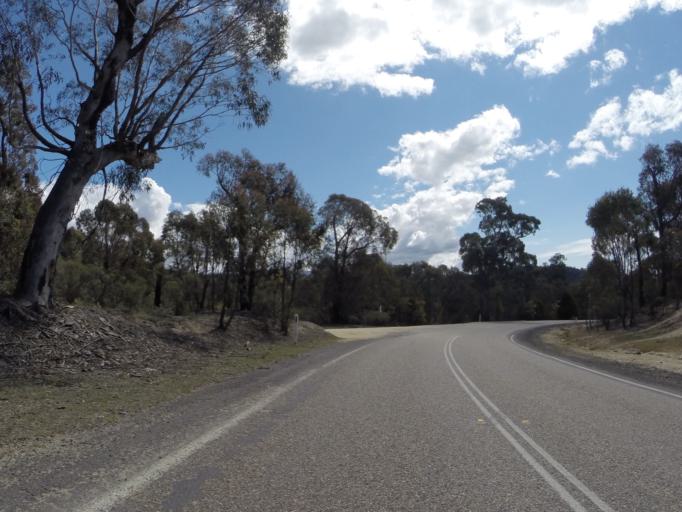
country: AU
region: Australian Capital Territory
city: Macquarie
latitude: -35.3456
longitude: 148.9301
